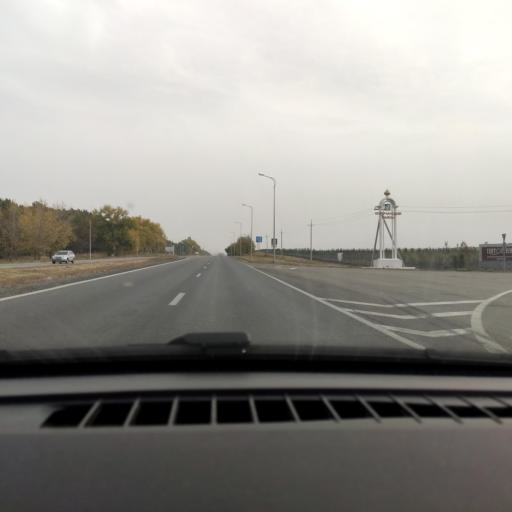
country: RU
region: Belgorod
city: Razumnoye
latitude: 50.6619
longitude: 36.7024
